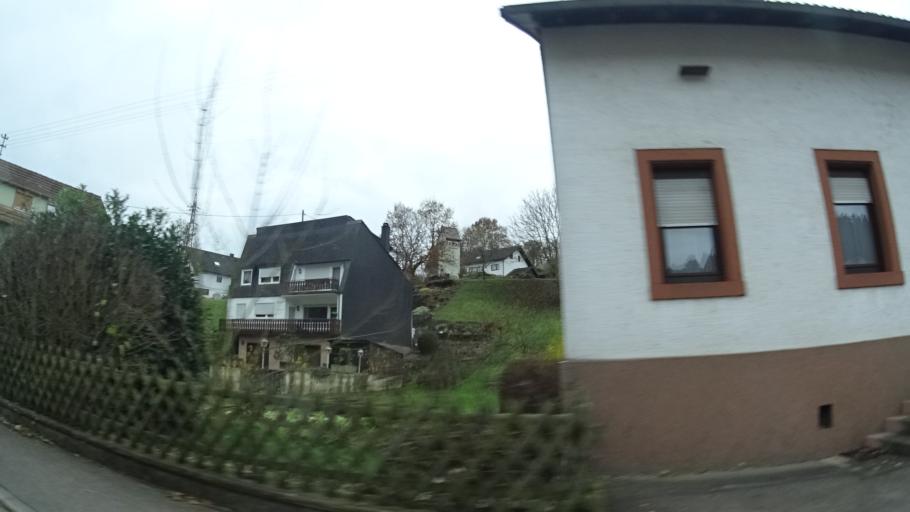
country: DE
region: Baden-Wuerttemberg
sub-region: Karlsruhe Region
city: Eberbach
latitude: 49.4272
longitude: 8.9563
